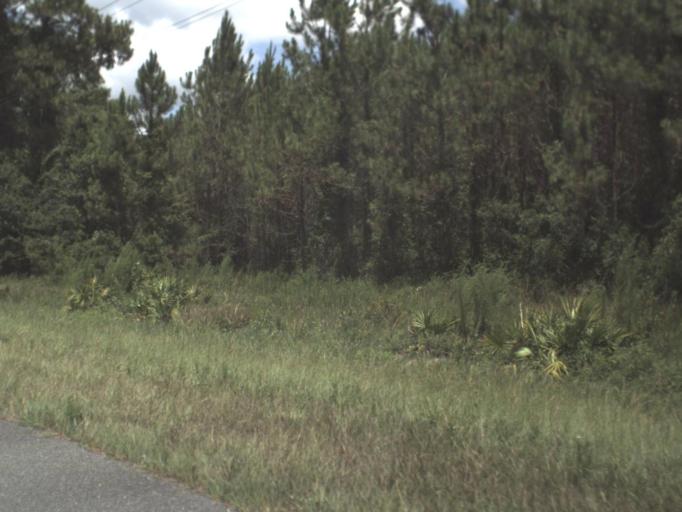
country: US
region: Florida
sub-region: Taylor County
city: Perry
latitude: 30.1427
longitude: -83.7966
